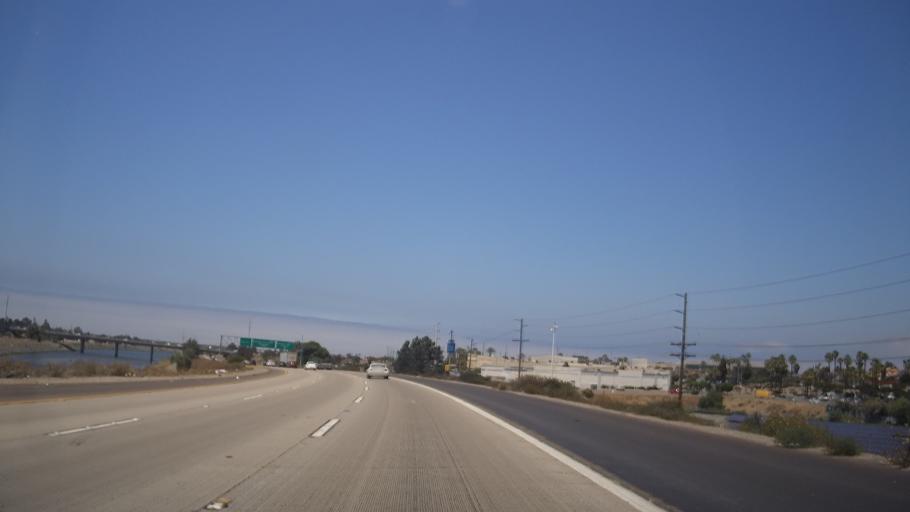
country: US
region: California
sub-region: San Diego County
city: Chula Vista
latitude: 32.6592
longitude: -117.0839
